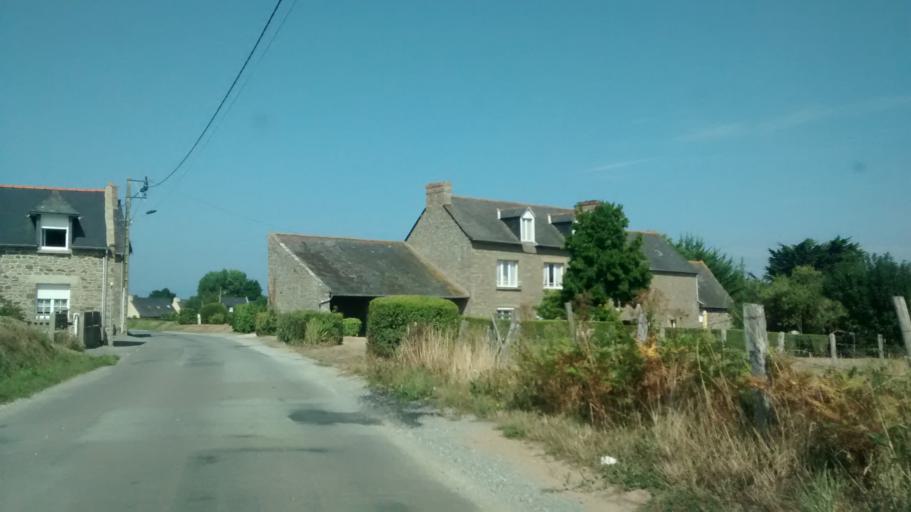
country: FR
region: Brittany
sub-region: Departement d'Ille-et-Vilaine
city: Saint-Coulomb
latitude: 48.6828
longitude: -1.8970
